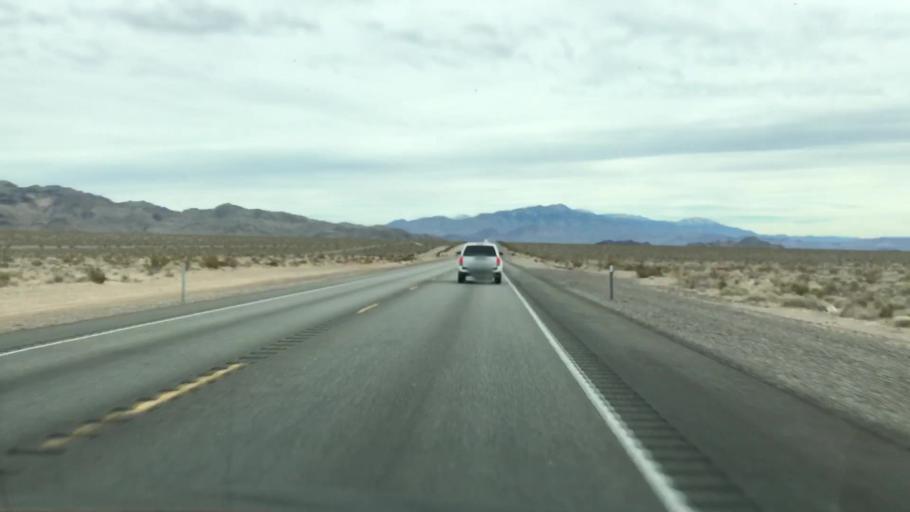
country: US
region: Nevada
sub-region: Nye County
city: Pahrump
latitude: 36.6088
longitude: -116.2667
